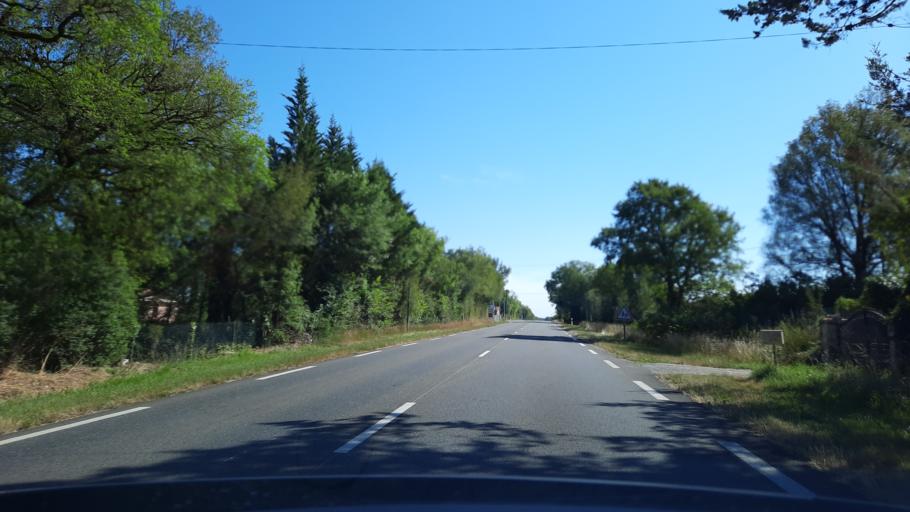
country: FR
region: Midi-Pyrenees
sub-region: Departement du Tarn-et-Garonne
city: Caylus
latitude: 44.2162
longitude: 1.7329
